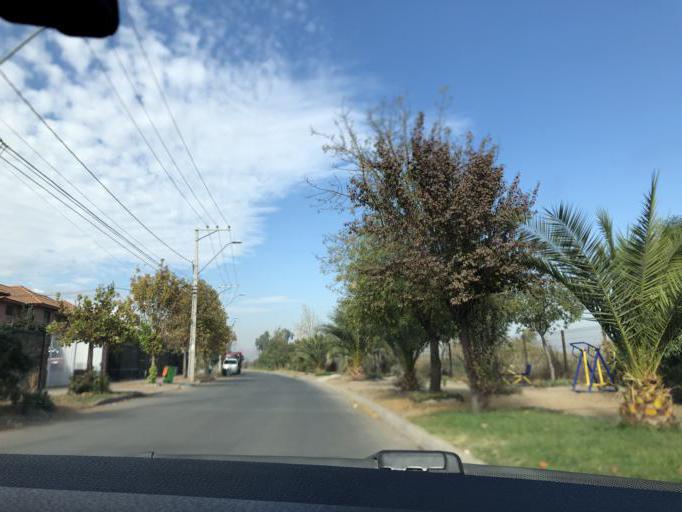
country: CL
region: Santiago Metropolitan
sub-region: Provincia de Cordillera
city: Puente Alto
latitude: -33.5763
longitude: -70.5432
